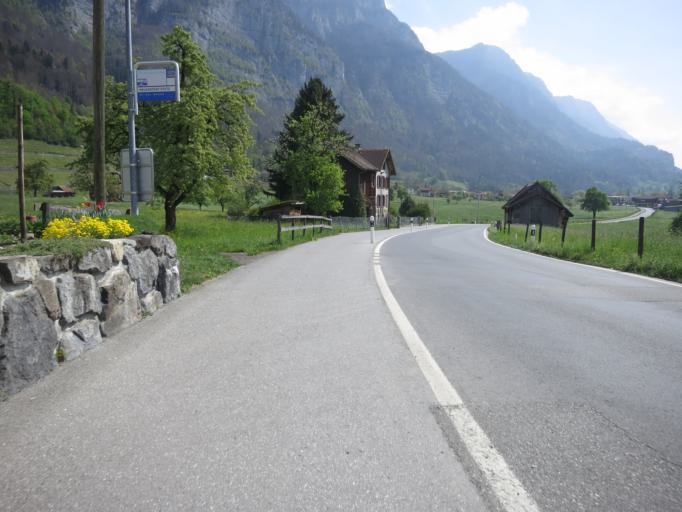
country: CH
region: Saint Gallen
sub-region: Wahlkreis Sarganserland
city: Walenstadt
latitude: 47.1197
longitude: 9.3260
